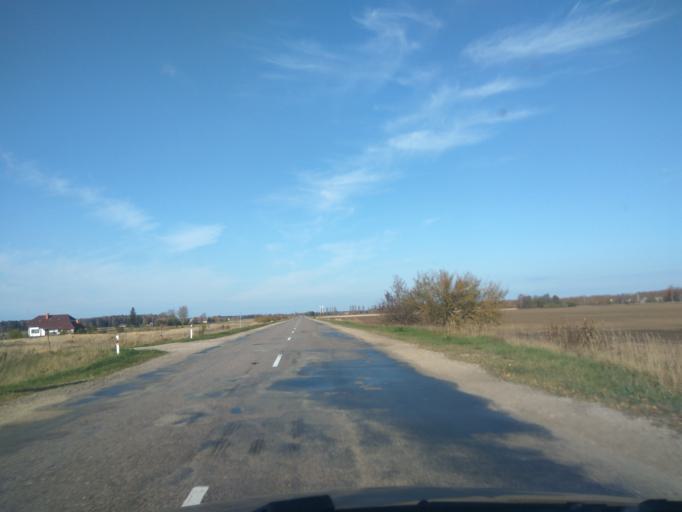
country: LV
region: Ventspils Rajons
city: Piltene
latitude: 57.2422
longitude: 21.5960
